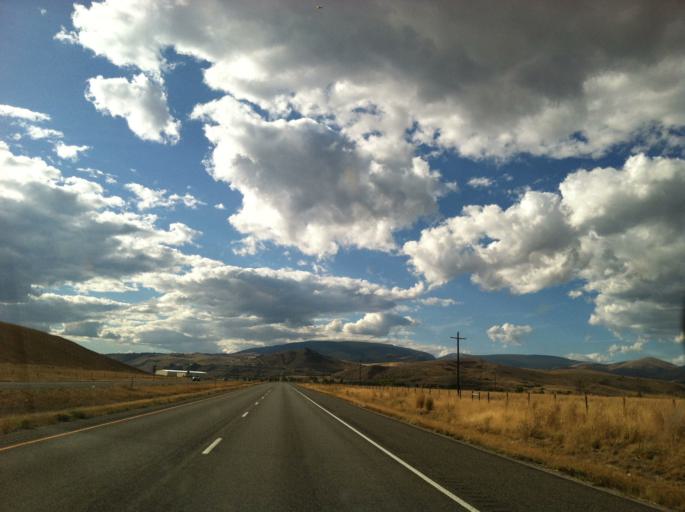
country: US
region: Montana
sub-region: Deer Lodge County
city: Anaconda
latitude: 46.1256
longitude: -112.8906
